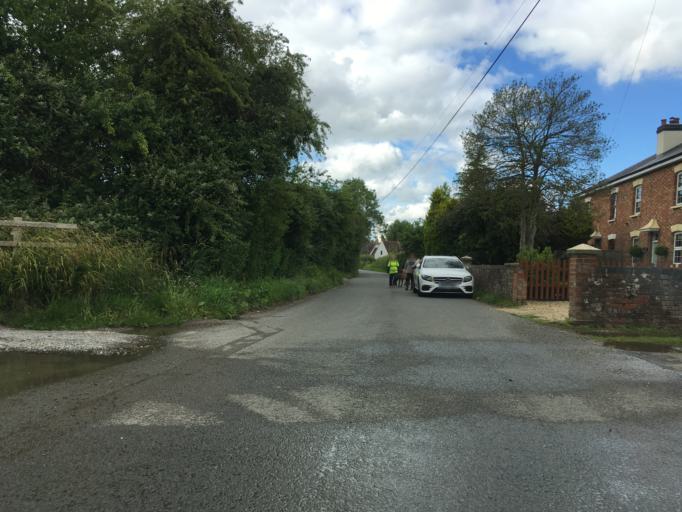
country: GB
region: England
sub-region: Gloucestershire
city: Stonehouse
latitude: 51.7977
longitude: -2.3442
